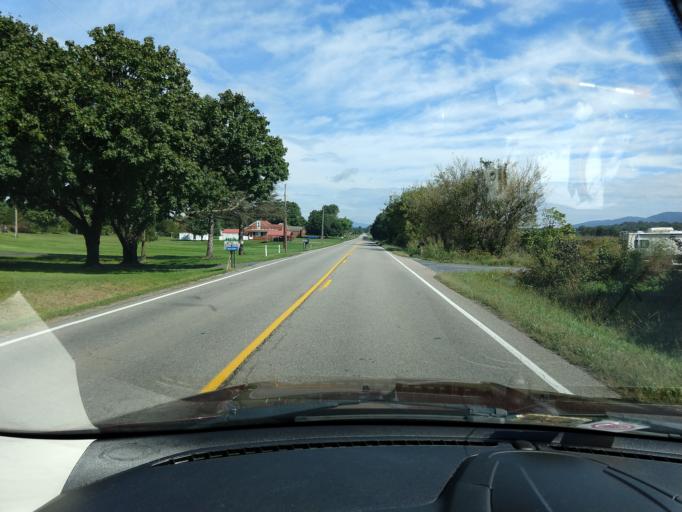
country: US
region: Virginia
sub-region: Augusta County
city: Crimora
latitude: 38.1906
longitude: -78.8397
